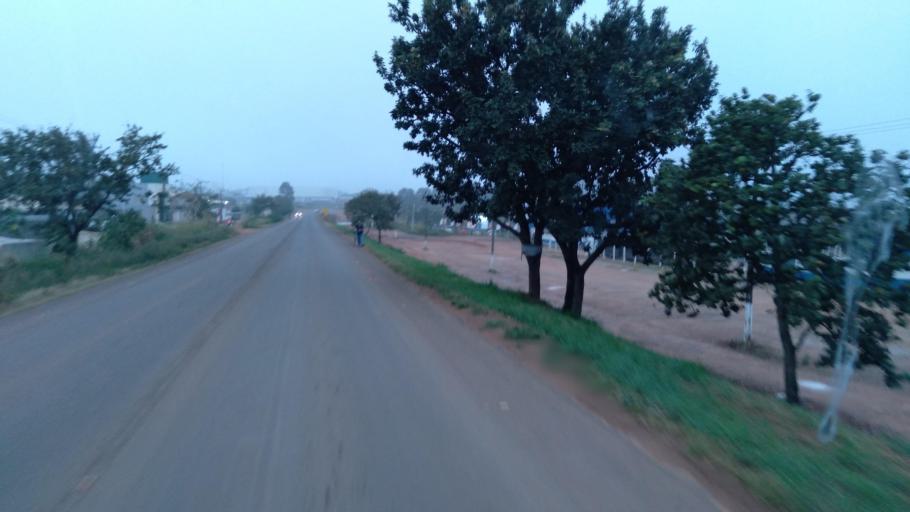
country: BR
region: Goias
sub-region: Mineiros
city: Mineiros
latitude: -17.5818
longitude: -52.5458
